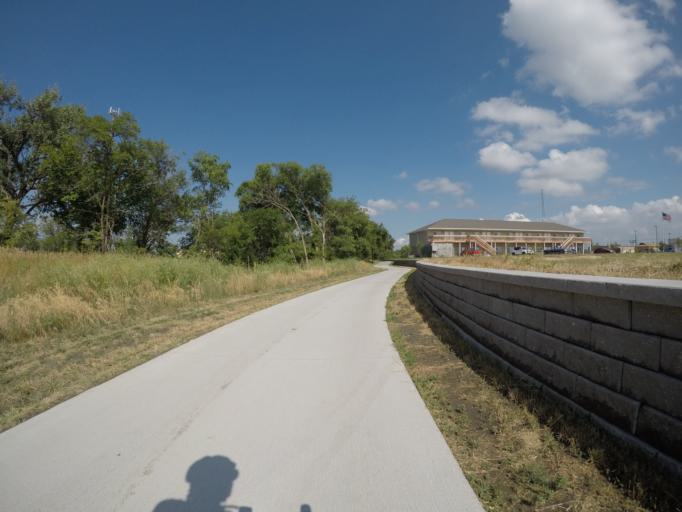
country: US
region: Nebraska
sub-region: Buffalo County
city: Kearney
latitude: 40.6760
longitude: -99.0895
